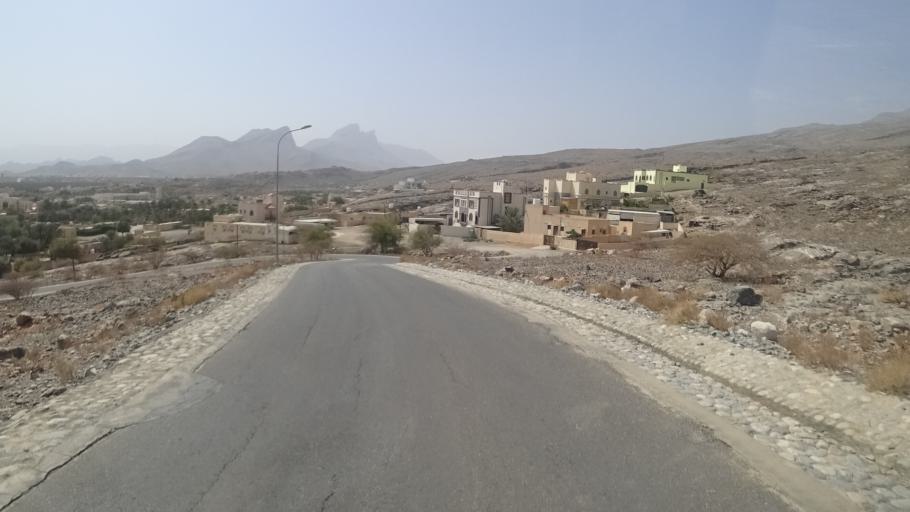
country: OM
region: Muhafazat ad Dakhiliyah
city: Bahla'
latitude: 23.1255
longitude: 57.2960
